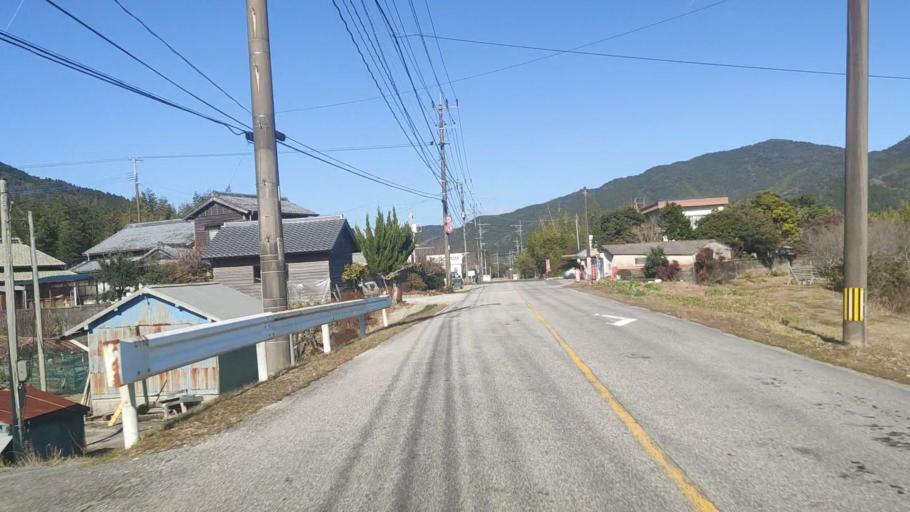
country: JP
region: Oita
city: Saiki
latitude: 32.9144
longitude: 131.9284
